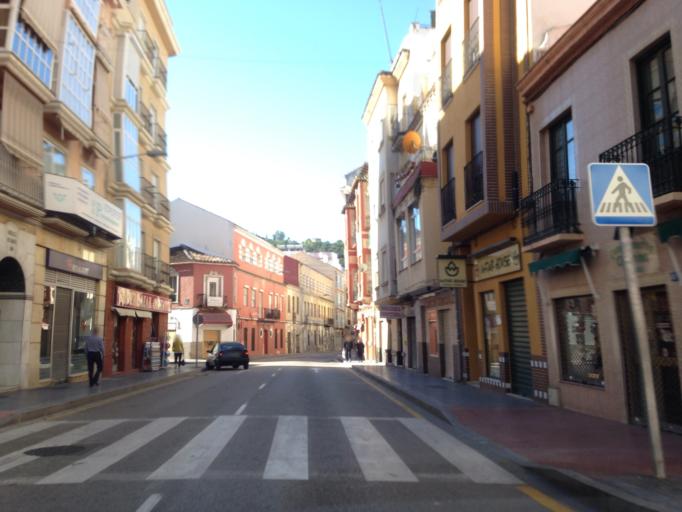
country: ES
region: Andalusia
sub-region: Provincia de Malaga
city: Malaga
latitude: 36.7291
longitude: -4.4146
